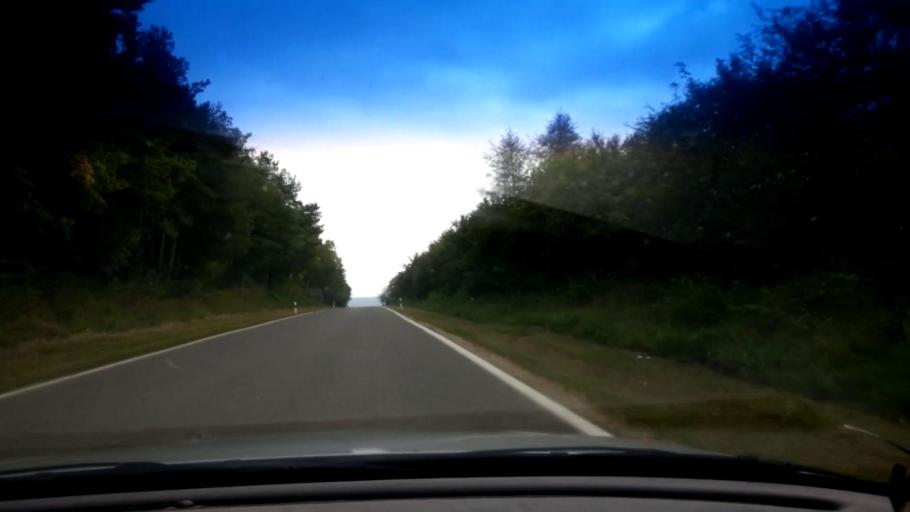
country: DE
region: Bavaria
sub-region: Upper Franconia
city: Memmelsdorf
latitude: 49.9770
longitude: 10.9692
